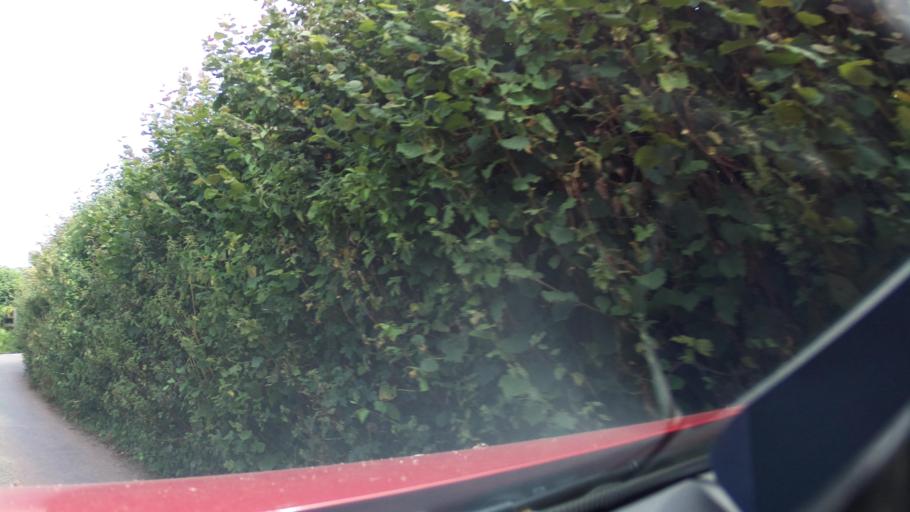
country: GB
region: England
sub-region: Devon
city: Marldon
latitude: 50.4152
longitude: -3.6231
